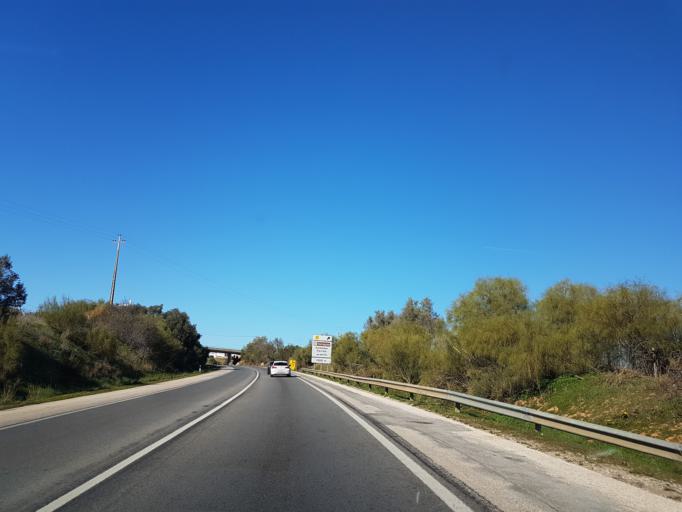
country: PT
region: Faro
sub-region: Lagoa
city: Estombar
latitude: 37.1501
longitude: -8.4806
